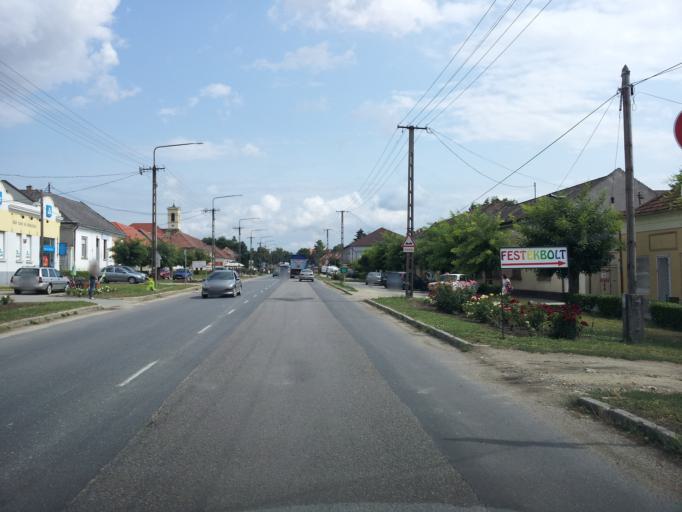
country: HU
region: Fejer
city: Enying
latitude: 46.9308
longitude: 18.2419
